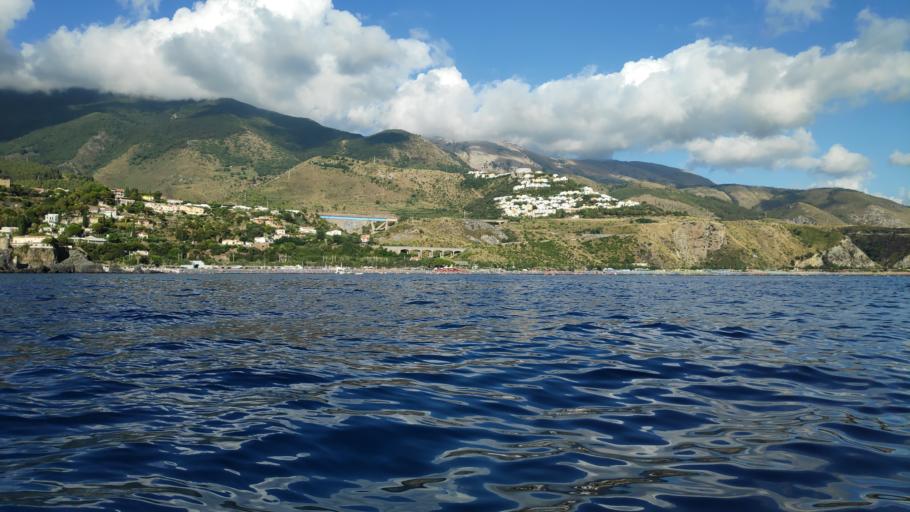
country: IT
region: Calabria
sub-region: Provincia di Cosenza
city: Praia a Mare
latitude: 39.8701
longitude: 15.7815
